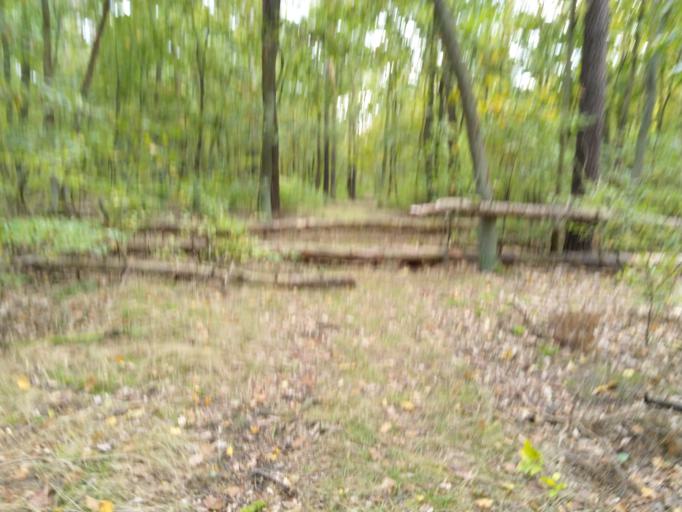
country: DE
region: Berlin
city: Rahnsdorf
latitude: 52.4528
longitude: 13.6603
